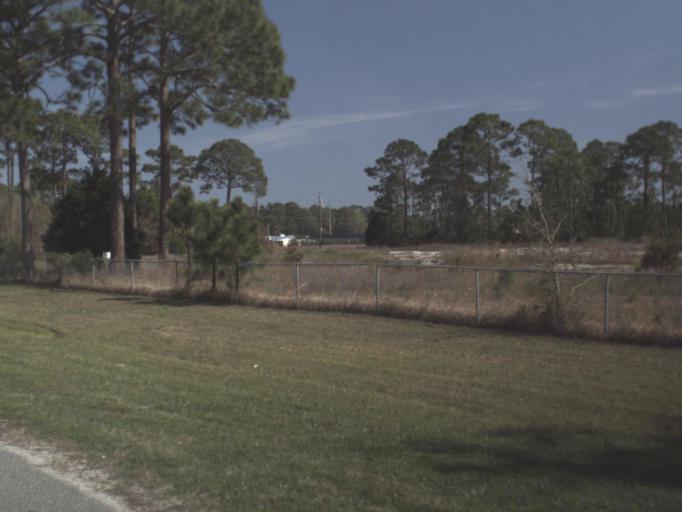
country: US
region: Florida
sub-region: Franklin County
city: Eastpoint
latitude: 29.7360
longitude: -84.8922
